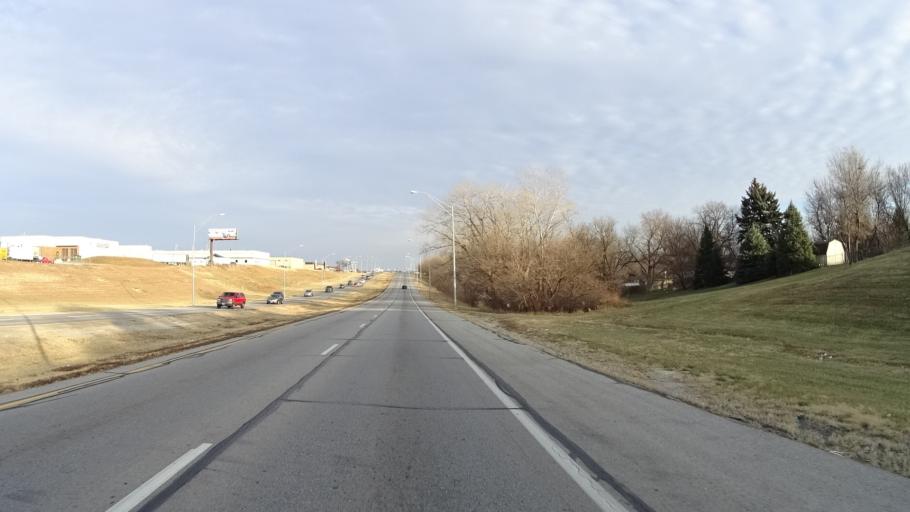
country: US
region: Nebraska
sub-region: Douglas County
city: Ralston
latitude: 41.2124
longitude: -96.0601
